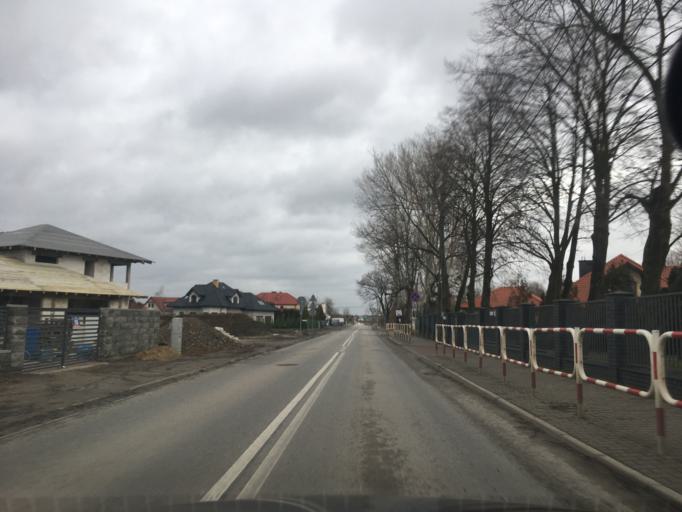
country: PL
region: Masovian Voivodeship
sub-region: Powiat pruszkowski
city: Rybie
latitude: 52.1276
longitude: 20.9619
